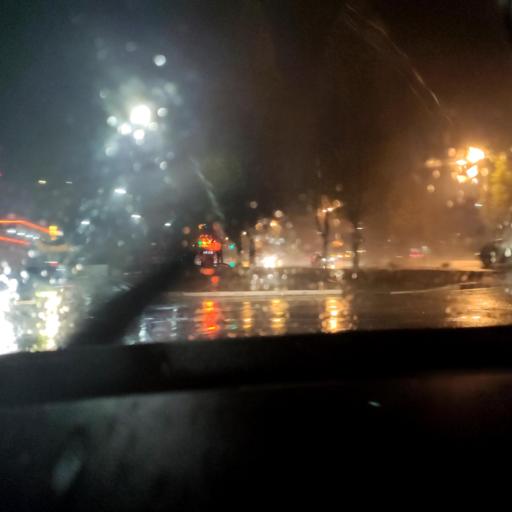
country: RU
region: Voronezj
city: Voronezh
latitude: 51.6456
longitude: 39.1308
